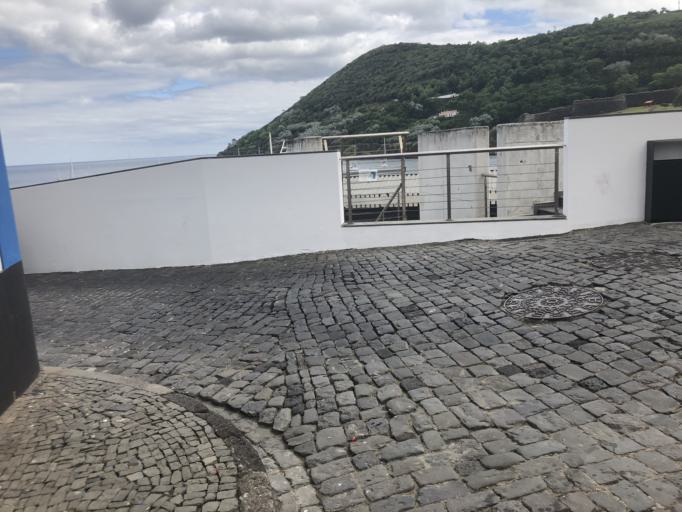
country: PT
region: Azores
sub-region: Angra do Heroismo
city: Angra do Heroismo
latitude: 38.6543
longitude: -27.2198
